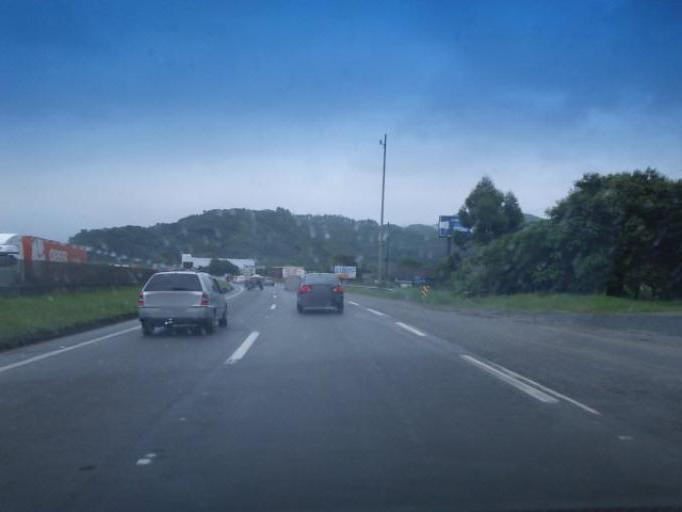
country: BR
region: Santa Catarina
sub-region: Penha
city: Penha
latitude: -26.8200
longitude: -48.6840
